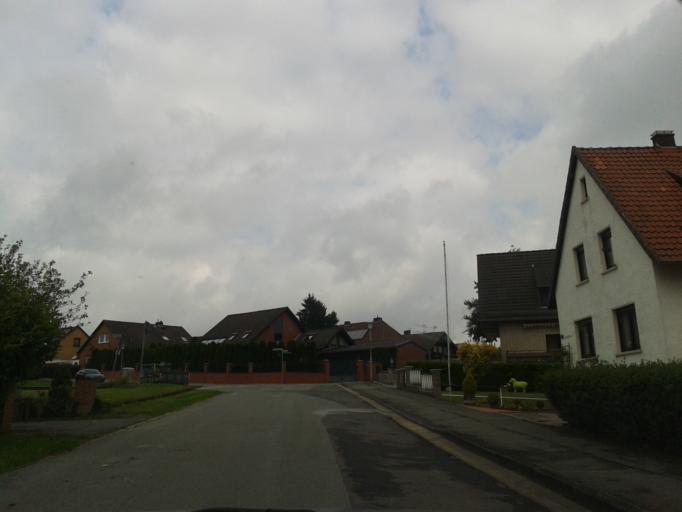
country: DE
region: North Rhine-Westphalia
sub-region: Regierungsbezirk Detmold
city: Lugde
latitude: 51.9772
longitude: 9.1925
